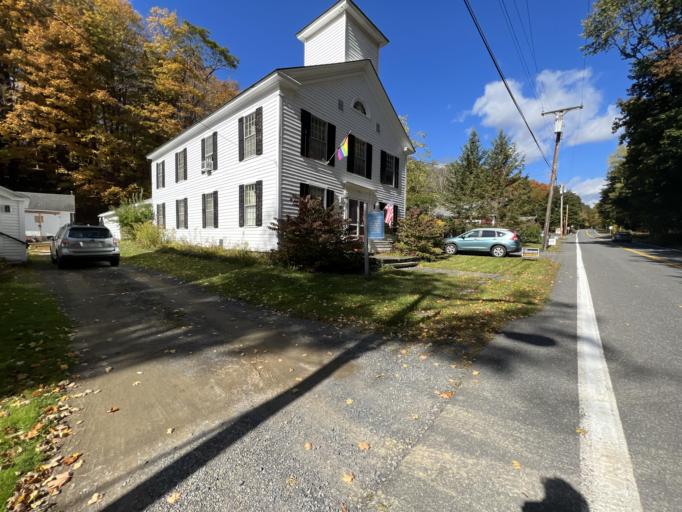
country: US
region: New York
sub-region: Schoharie County
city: Middleburgh
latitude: 42.5178
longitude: -74.1385
